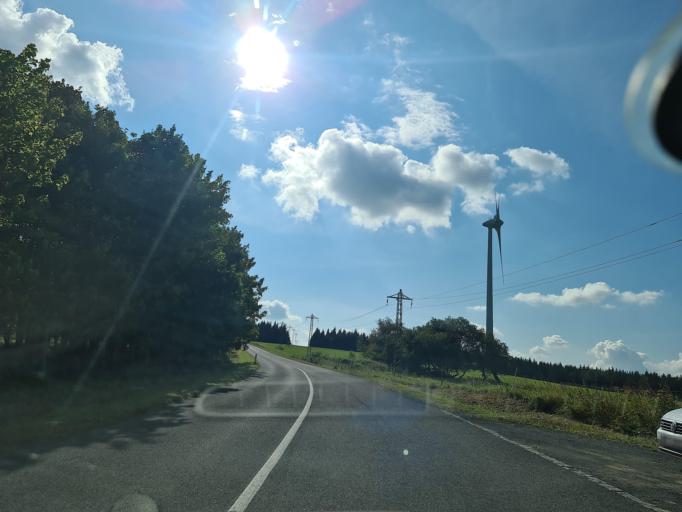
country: CZ
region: Ustecky
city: Mezibori
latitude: 50.6385
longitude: 13.5473
